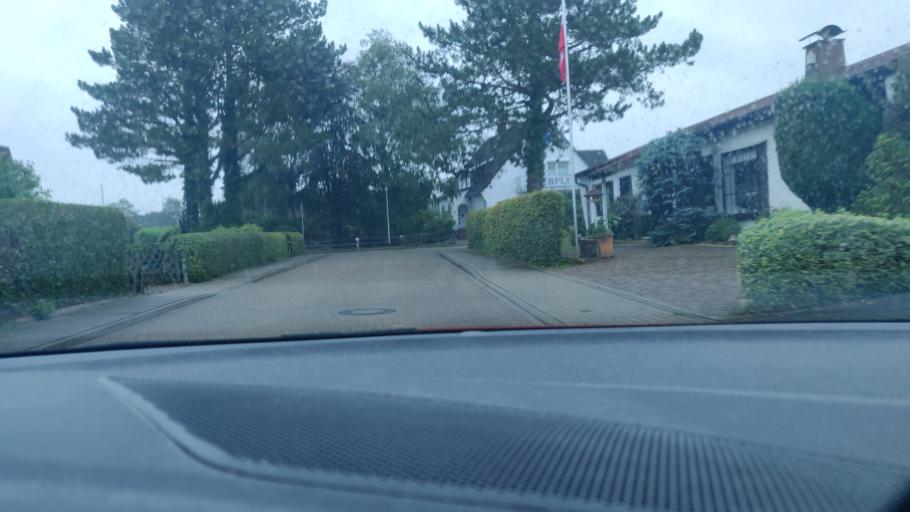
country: DE
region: Lower Saxony
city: Cuxhaven
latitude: 53.8625
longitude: 8.6128
